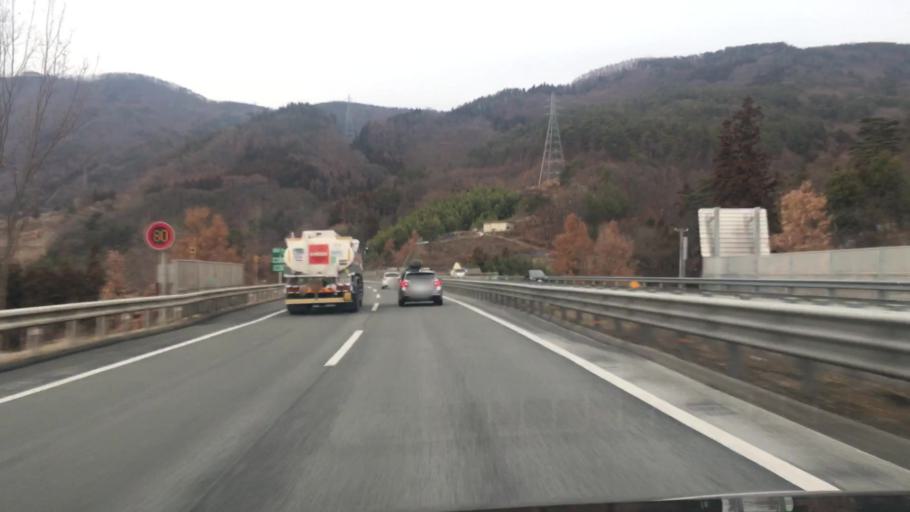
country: JP
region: Nagano
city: Ueda
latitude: 36.4695
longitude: 138.1982
